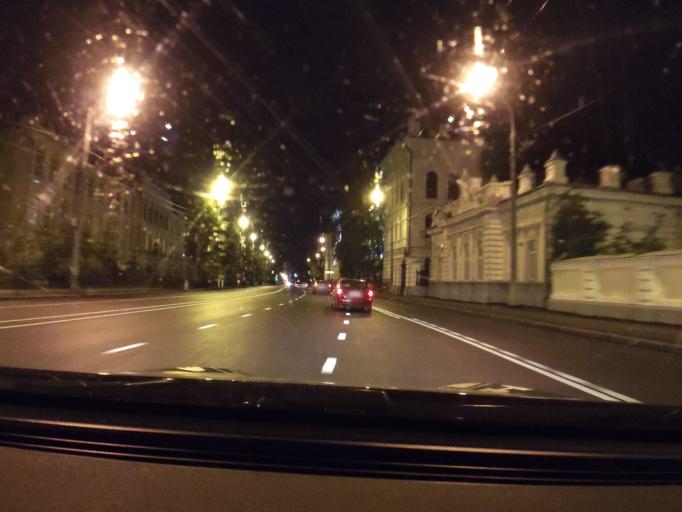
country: RU
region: Tatarstan
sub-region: Gorod Kazan'
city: Kazan
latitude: 55.7946
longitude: 49.1428
